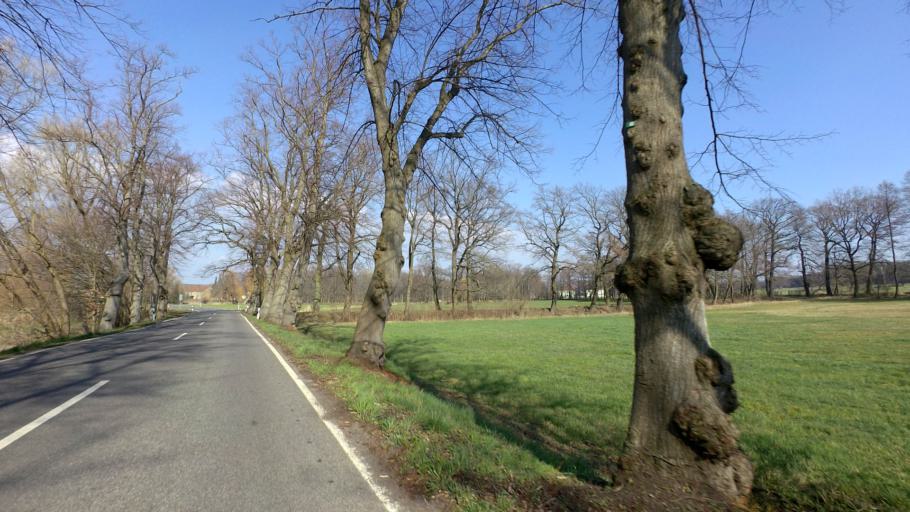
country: DE
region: Brandenburg
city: Dahme
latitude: 51.9006
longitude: 13.4866
